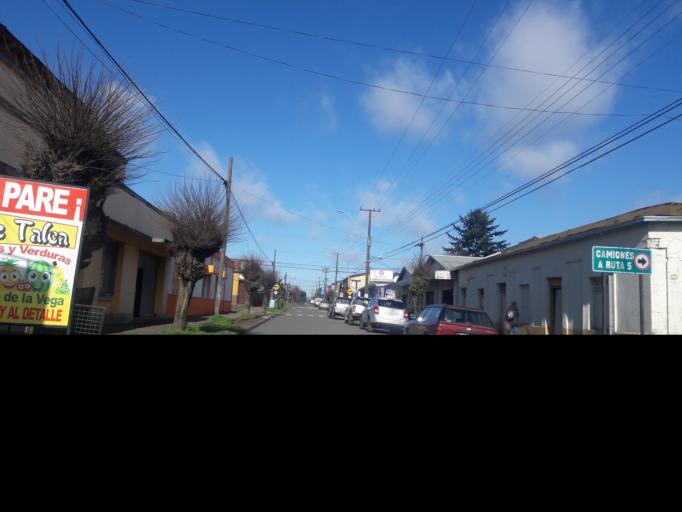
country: CL
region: Araucania
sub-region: Provincia de Malleco
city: Victoria
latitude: -38.2360
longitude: -72.3295
